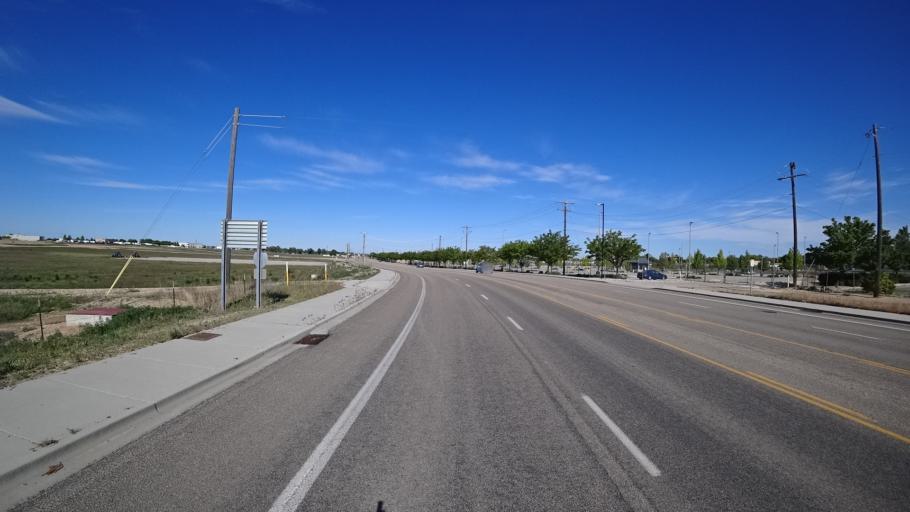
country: US
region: Idaho
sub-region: Ada County
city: Garden City
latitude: 43.5752
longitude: -116.2484
